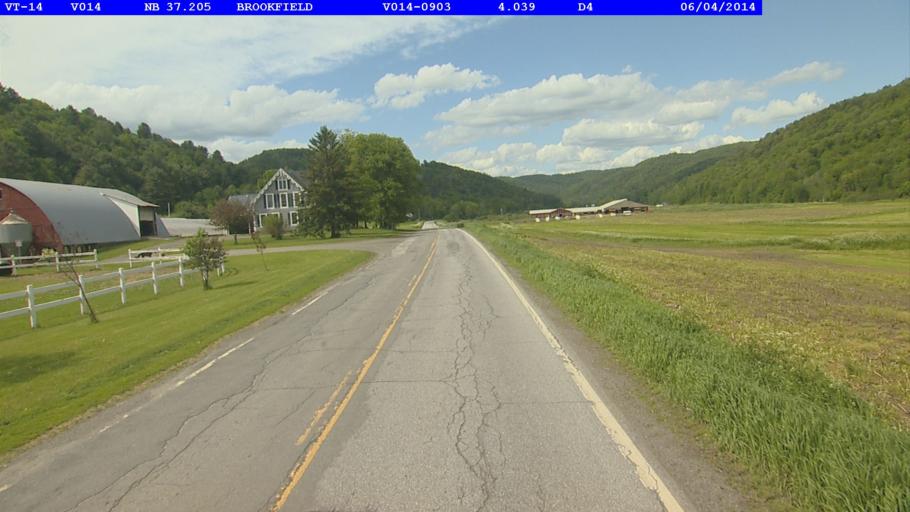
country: US
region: Vermont
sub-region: Orange County
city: Williamstown
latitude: 44.0351
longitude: -72.5692
